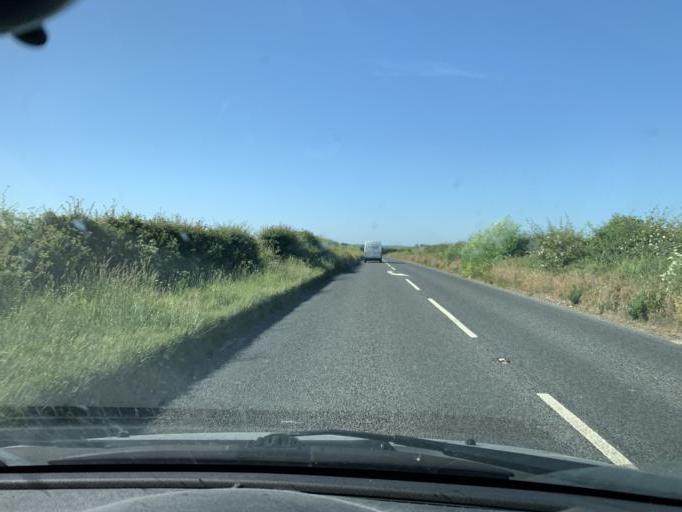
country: GB
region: England
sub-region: Wiltshire
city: Durnford
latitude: 51.1184
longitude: -1.7890
